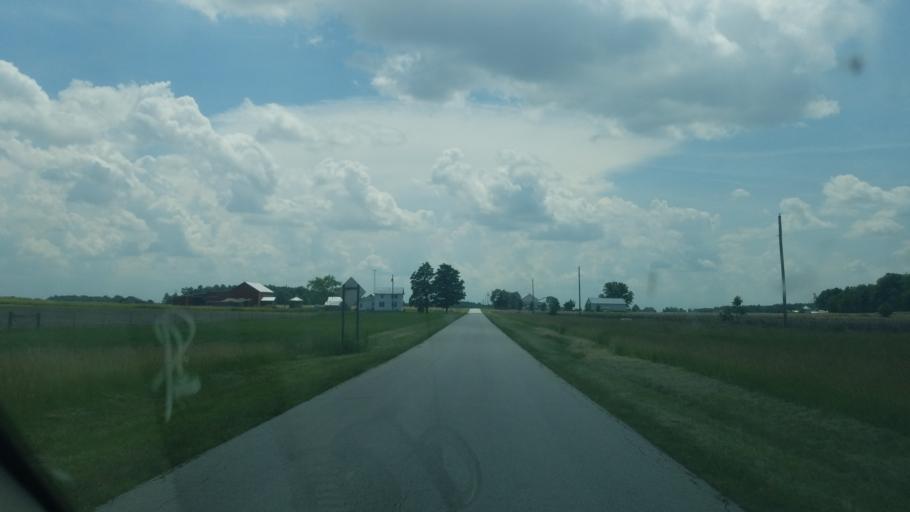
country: US
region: Ohio
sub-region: Hancock County
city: Arlington
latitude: 40.8267
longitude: -83.6001
